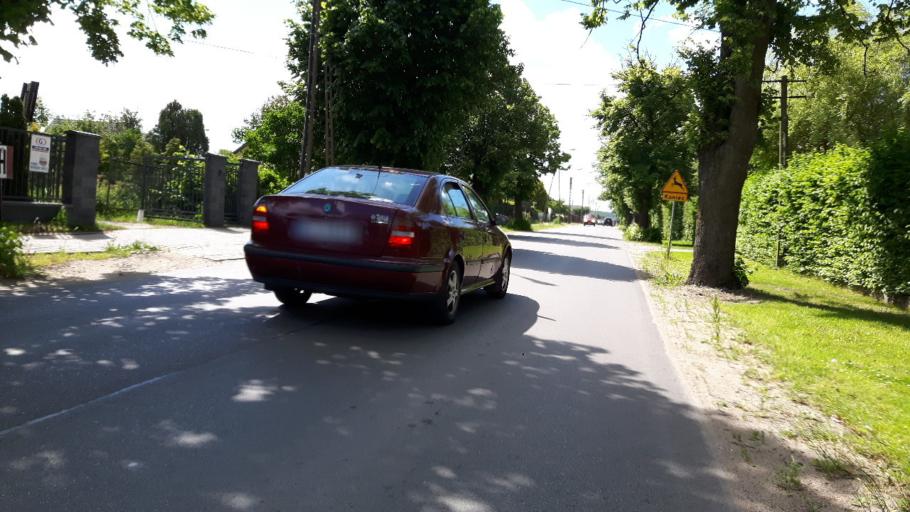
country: PL
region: Pomeranian Voivodeship
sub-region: Powiat pucki
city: Mosty
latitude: 54.6005
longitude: 18.4985
